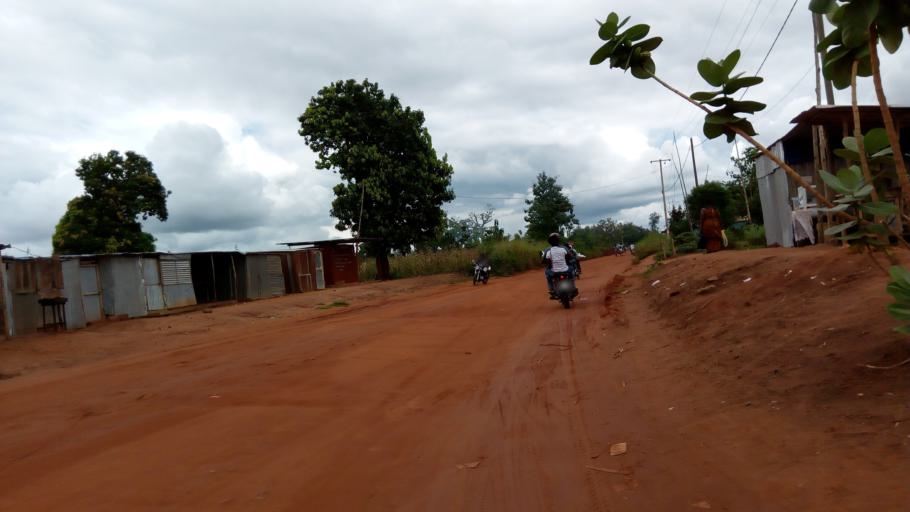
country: TG
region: Maritime
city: Tsevie
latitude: 6.2893
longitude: 1.1378
